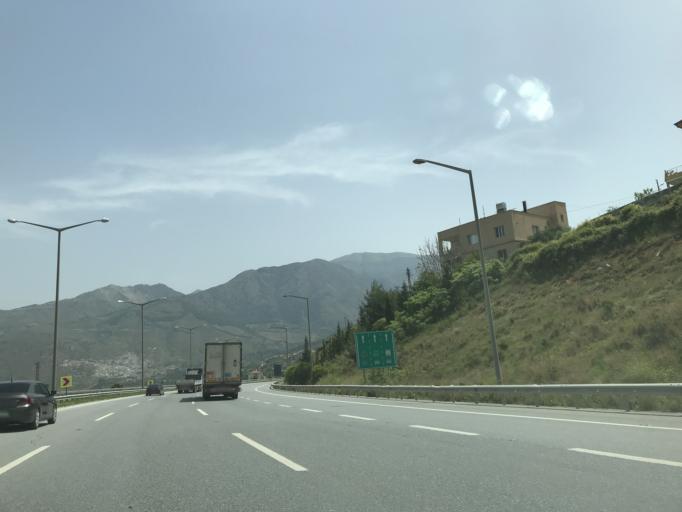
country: TR
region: Hatay
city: Iskenderun
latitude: 36.5644
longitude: 36.1766
